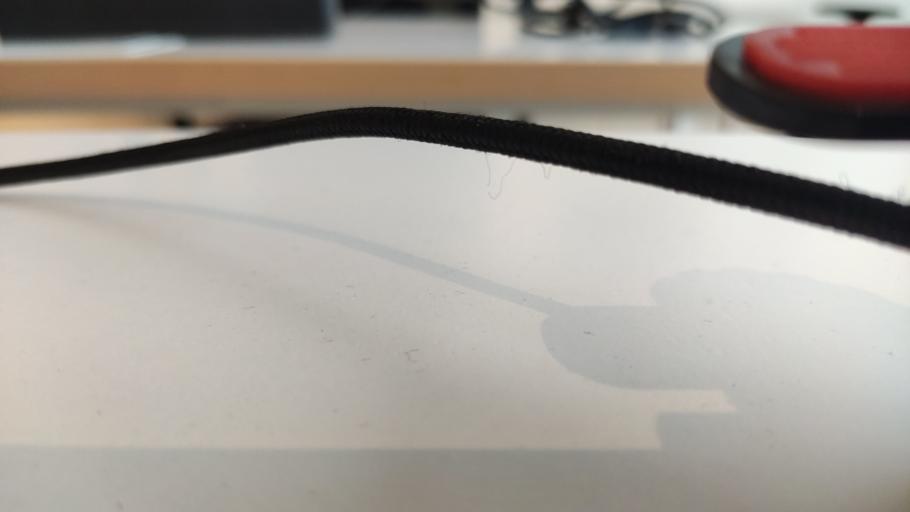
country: RU
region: Moskovskaya
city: Klin
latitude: 56.3270
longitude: 36.7019
